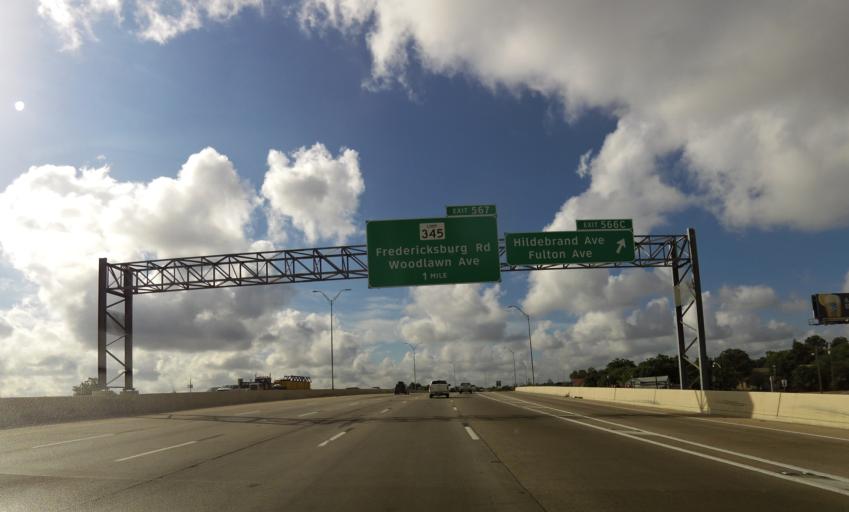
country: US
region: Texas
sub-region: Bexar County
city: Olmos Park
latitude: 29.4753
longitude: -98.5183
